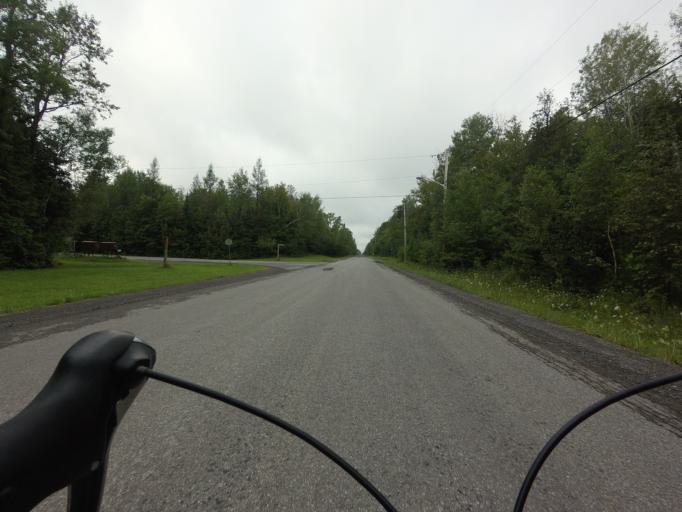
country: CA
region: Ontario
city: Bells Corners
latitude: 45.0327
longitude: -75.7534
